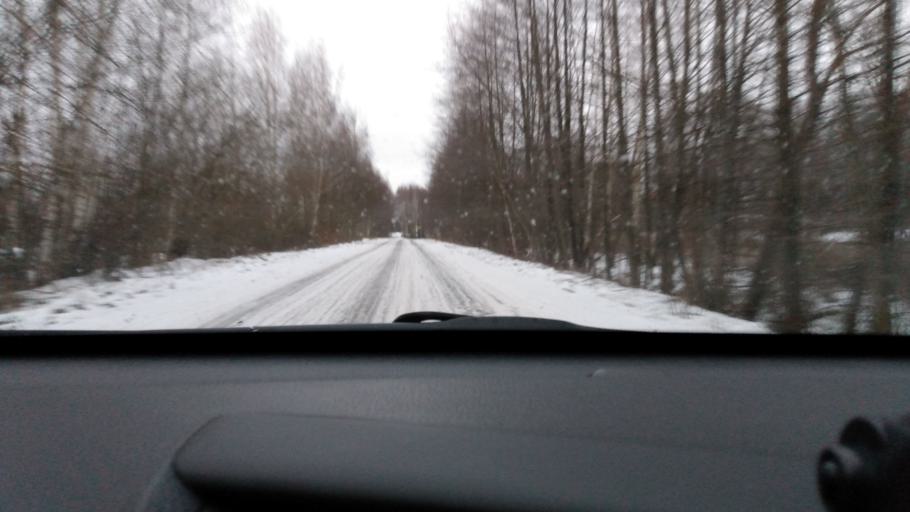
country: RU
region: Moskovskaya
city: Meshcherino
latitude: 55.3169
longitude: 38.3411
